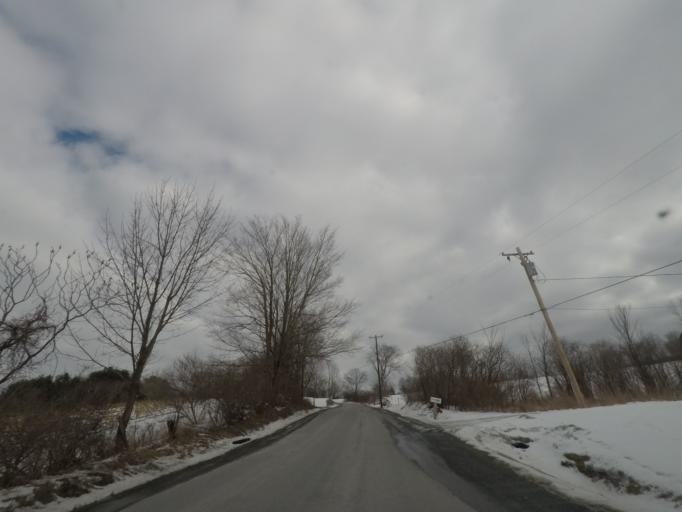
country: US
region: New York
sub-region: Rensselaer County
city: Hoosick Falls
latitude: 42.8732
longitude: -73.3999
